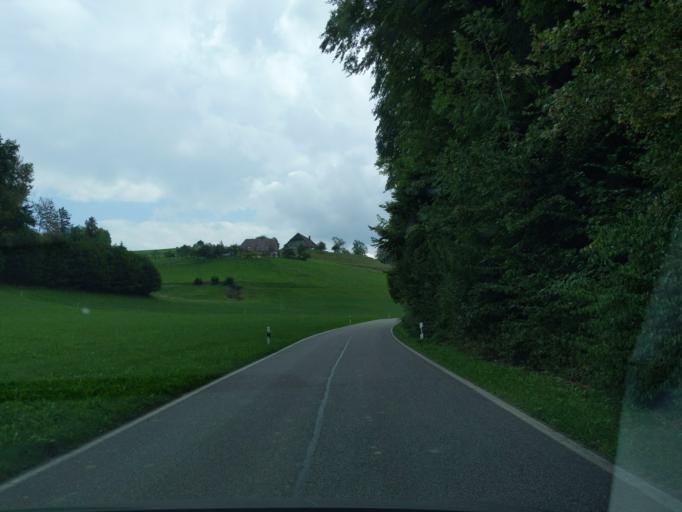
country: CH
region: Bern
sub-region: Oberaargau
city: Wyssachen
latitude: 47.0720
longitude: 7.8319
